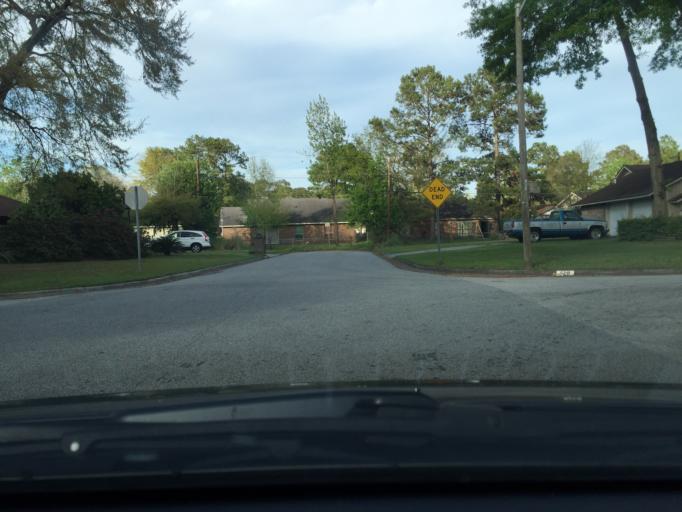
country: US
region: Georgia
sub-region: Chatham County
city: Montgomery
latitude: 32.0002
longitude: -81.1414
